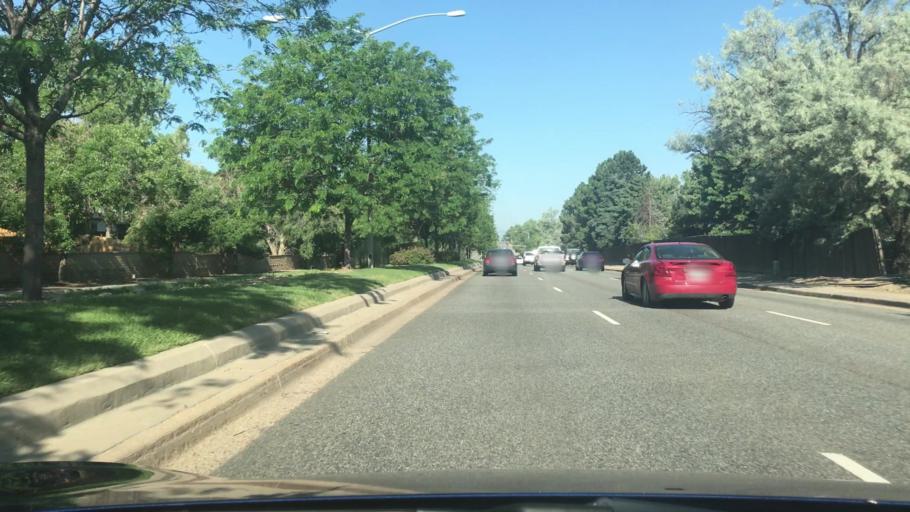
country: US
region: Colorado
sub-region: Arapahoe County
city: Dove Valley
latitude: 39.6531
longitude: -104.7935
